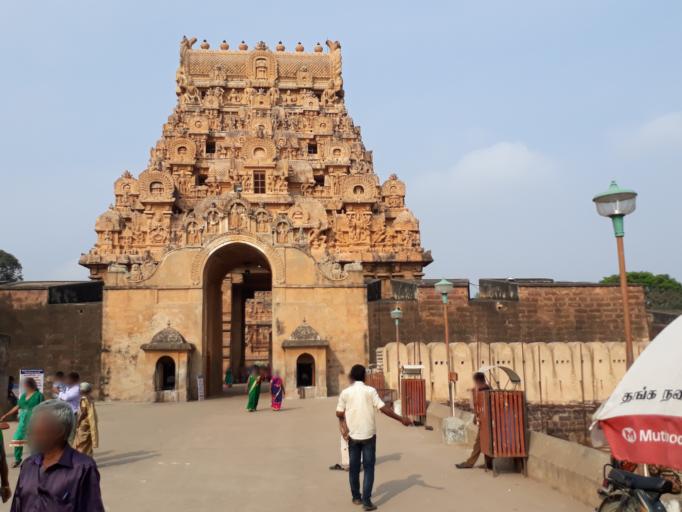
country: IN
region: Tamil Nadu
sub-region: Thanjavur
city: Thanjavur
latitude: 10.7835
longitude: 79.1339
